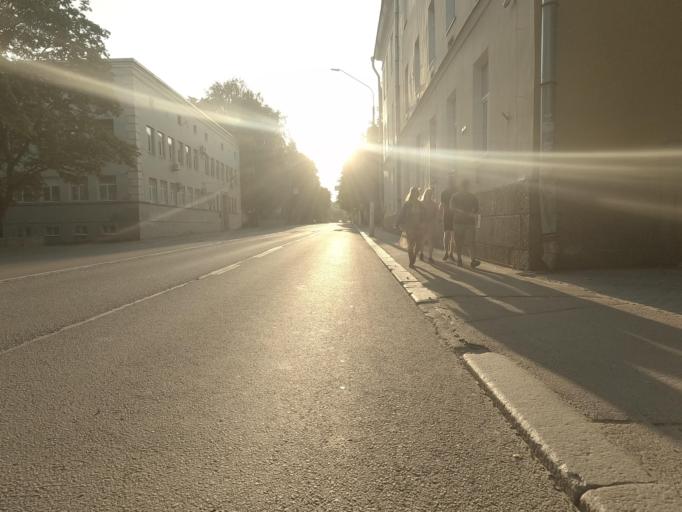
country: RU
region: Leningrad
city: Vyborg
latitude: 60.7099
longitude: 28.7638
